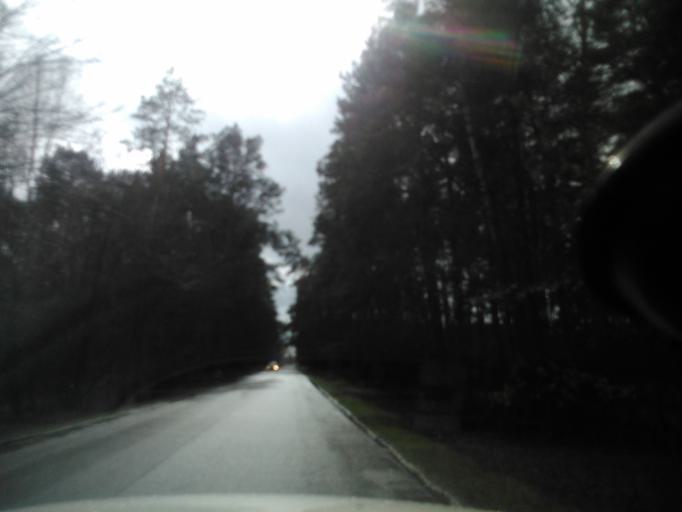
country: PL
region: Warmian-Masurian Voivodeship
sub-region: Powiat dzialdowski
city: Lidzbark
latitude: 53.2814
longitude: 19.8459
